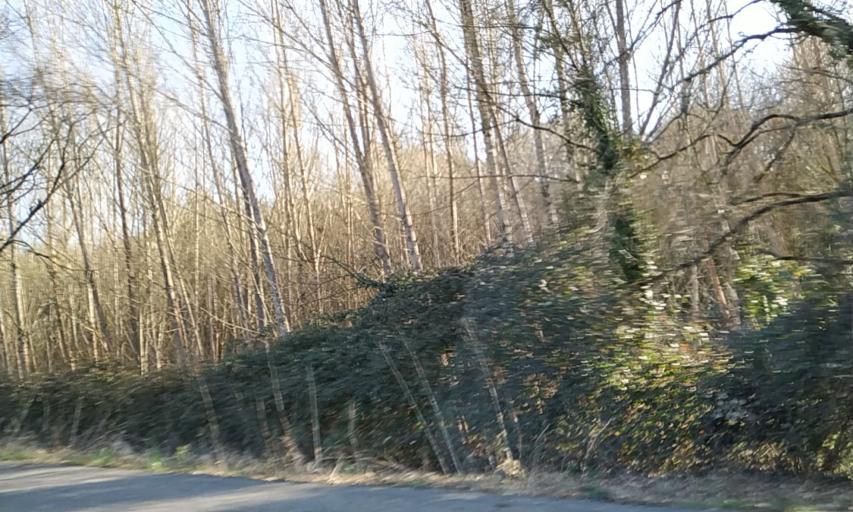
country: ES
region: Galicia
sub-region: Provincia de Lugo
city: Corgo
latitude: 42.9602
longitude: -7.4768
